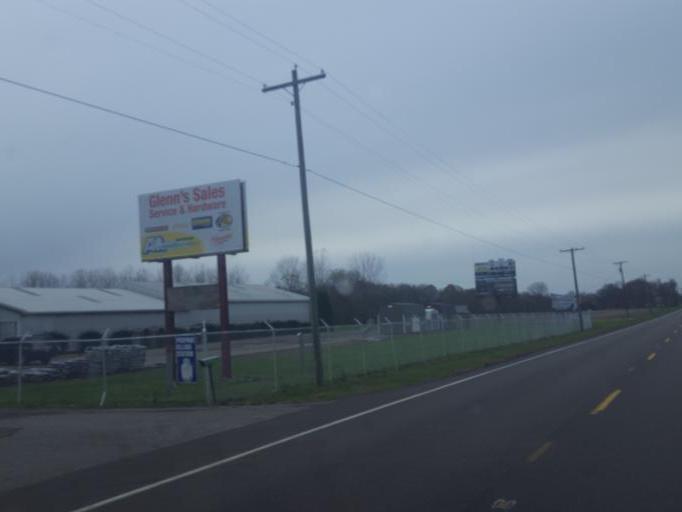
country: US
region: Ohio
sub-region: Knox County
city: Fredericktown
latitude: 40.4505
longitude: -82.5384
